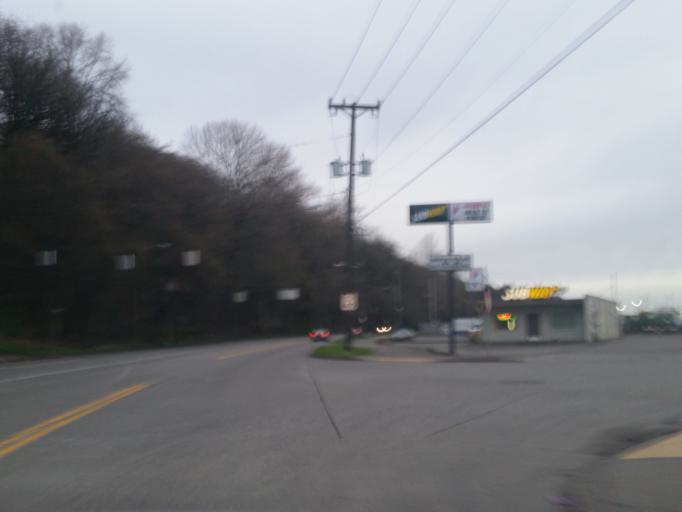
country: US
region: Washington
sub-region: King County
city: White Center
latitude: 47.5409
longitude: -122.3428
